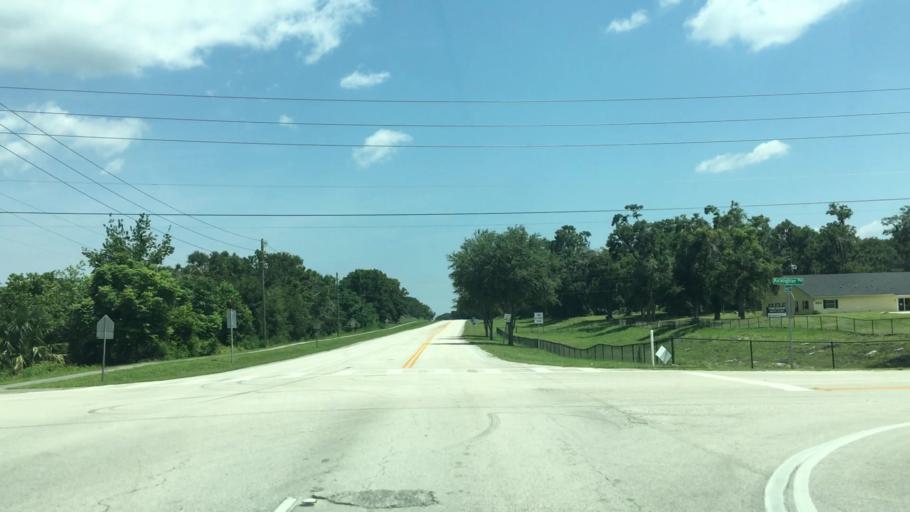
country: US
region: Florida
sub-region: Volusia County
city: Lake Helen
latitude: 28.9701
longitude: -81.2236
